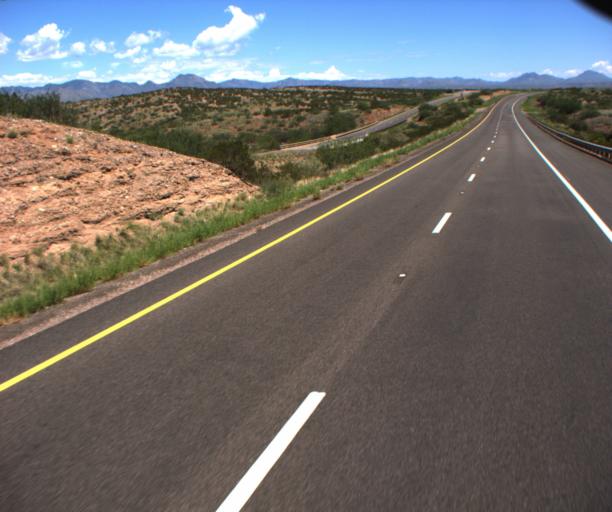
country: US
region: Arizona
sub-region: Greenlee County
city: Clifton
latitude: 32.9831
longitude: -109.2612
